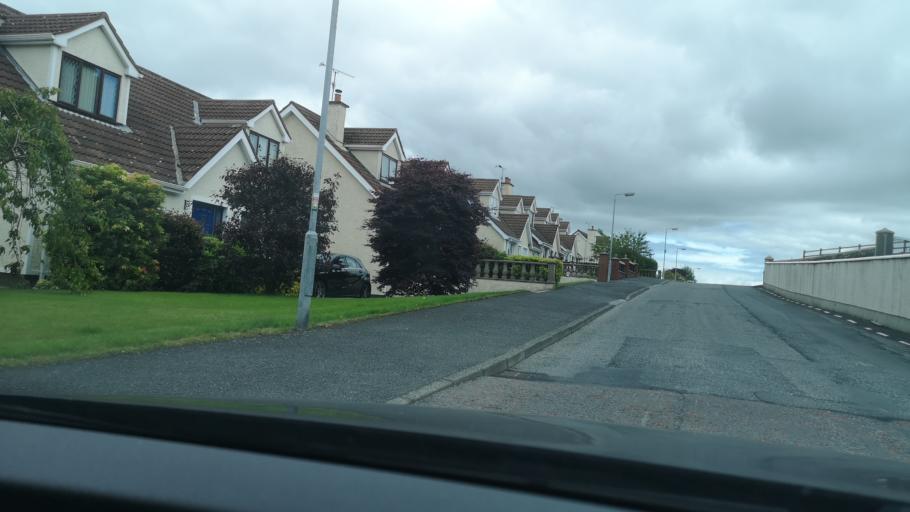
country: GB
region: Northern Ireland
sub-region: Newry and Mourne District
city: Newry
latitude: 54.1722
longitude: -6.3282
